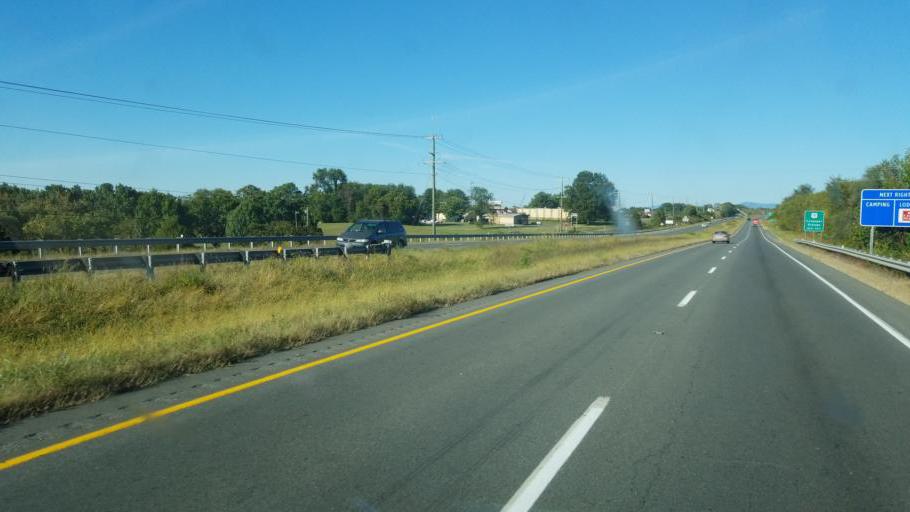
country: US
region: Virginia
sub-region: Culpeper County
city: Culpeper
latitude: 38.4452
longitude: -77.9960
